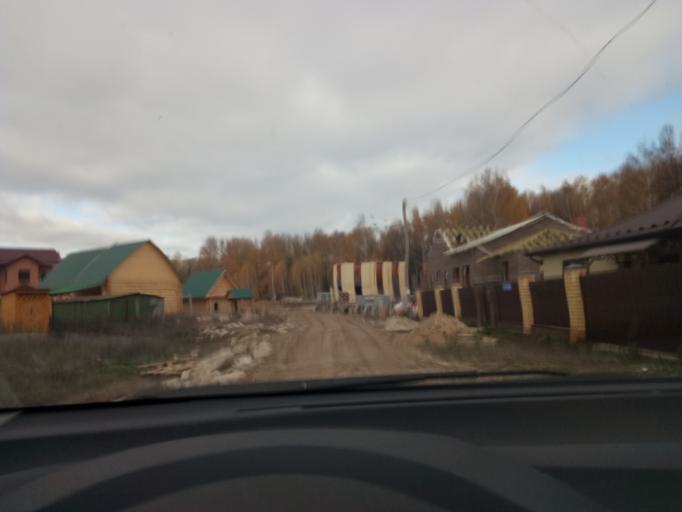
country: RU
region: Tatarstan
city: Staroye Arakchino
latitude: 55.9693
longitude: 49.0453
